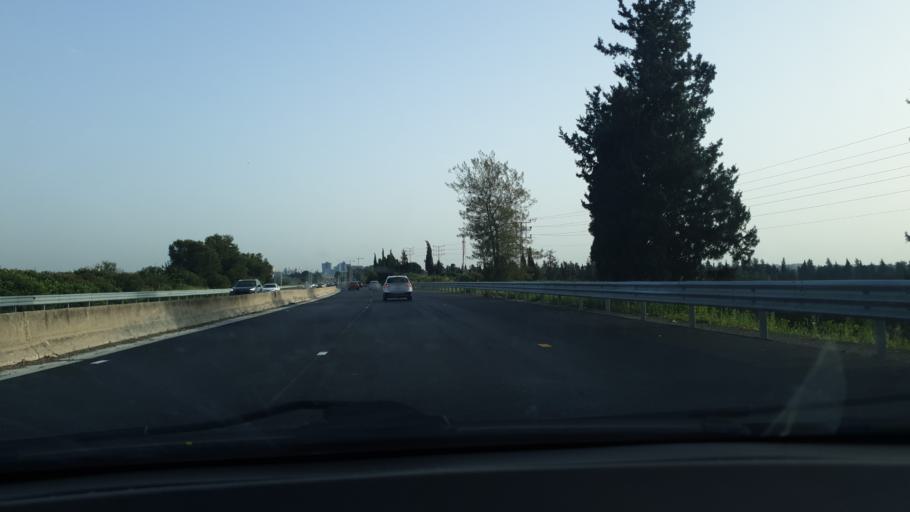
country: IL
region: Central District
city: Tel Mond
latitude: 32.2258
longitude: 34.8828
